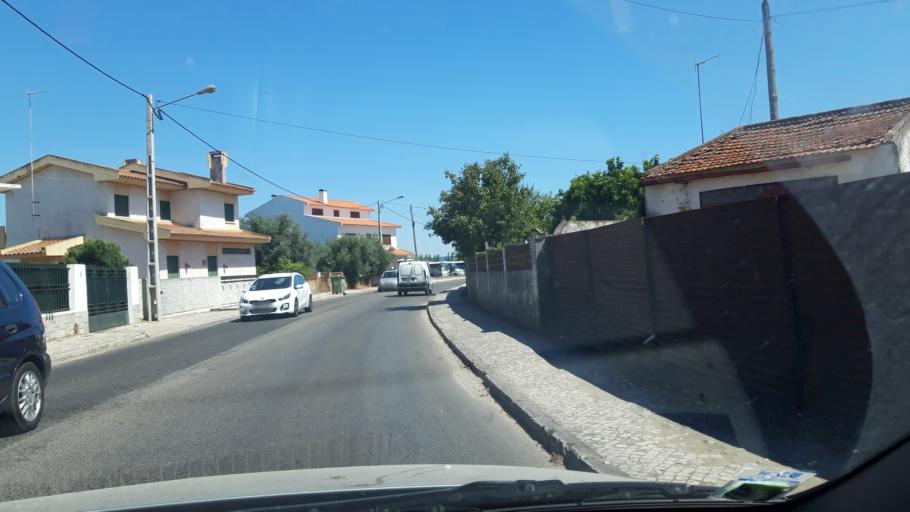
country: PT
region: Santarem
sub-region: Entroncamento
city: Entroncamento
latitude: 39.4654
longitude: -8.4648
